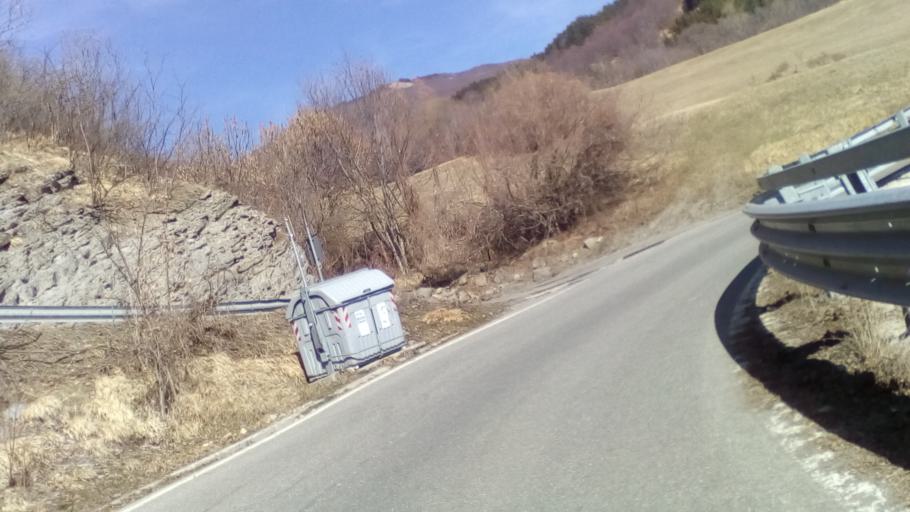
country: IT
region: Emilia-Romagna
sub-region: Provincia di Modena
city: Riolunato
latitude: 44.2569
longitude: 10.6385
